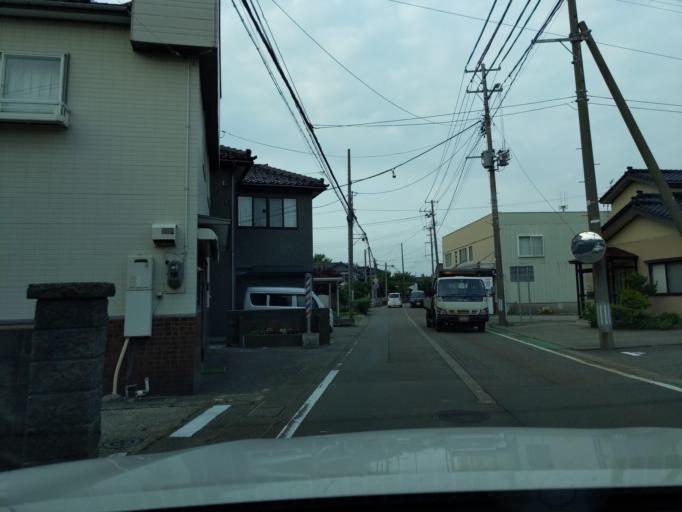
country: JP
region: Niigata
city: Kashiwazaki
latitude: 37.3829
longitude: 138.5736
